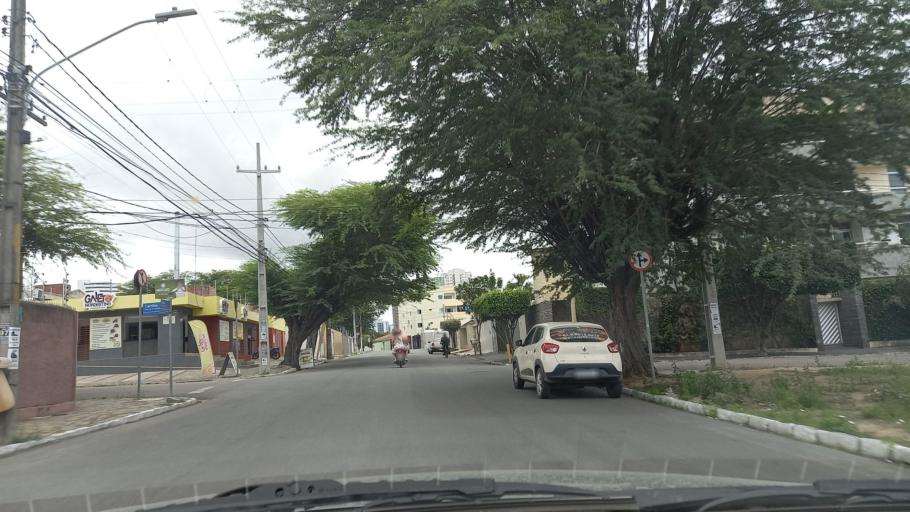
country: BR
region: Pernambuco
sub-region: Caruaru
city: Caruaru
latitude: -8.2764
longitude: -35.9678
